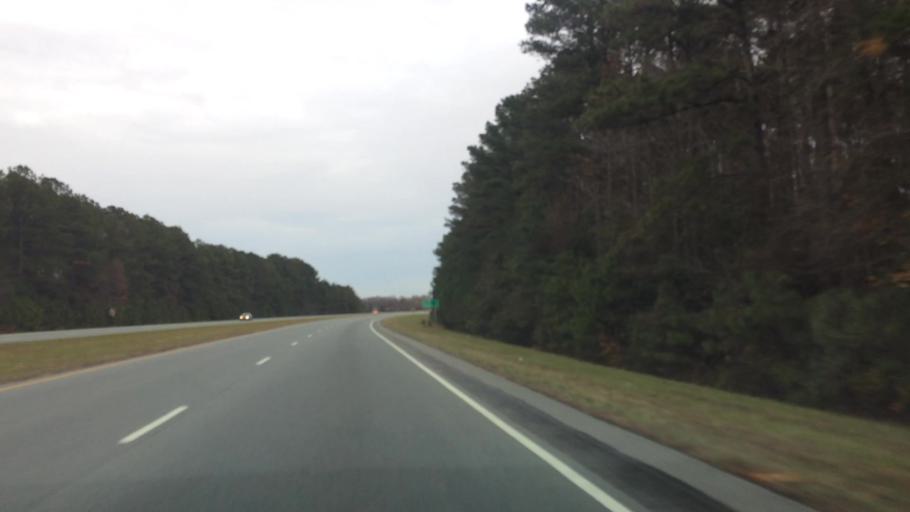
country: US
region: North Carolina
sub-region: Wayne County
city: Mount Olive
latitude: 35.1196
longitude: -78.1801
